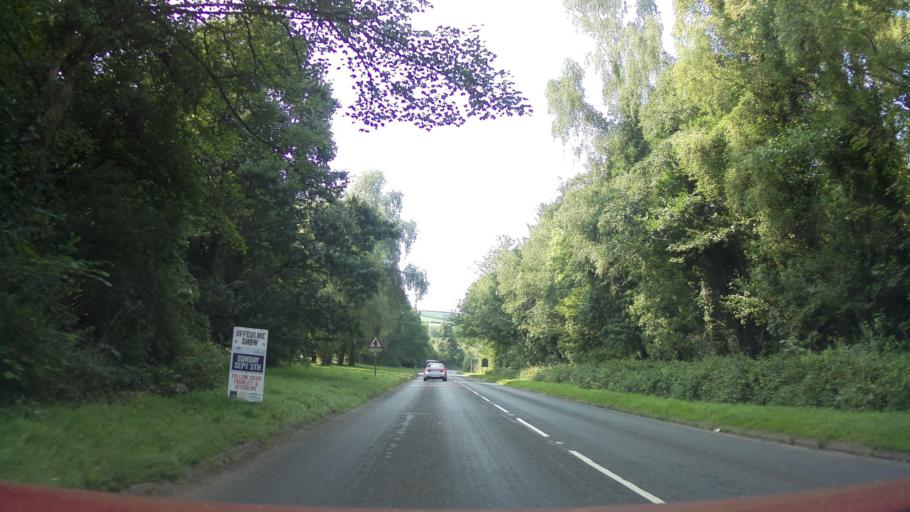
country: GB
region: England
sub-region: Devon
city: Tiverton
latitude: 50.8867
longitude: -3.4945
